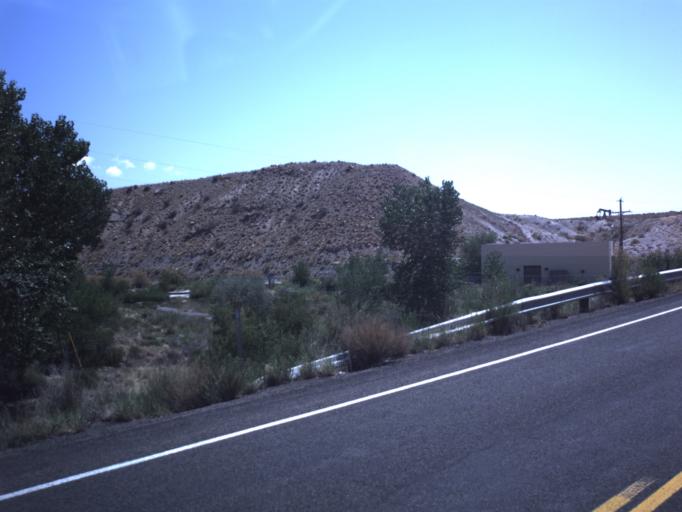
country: US
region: Utah
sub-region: Emery County
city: Orangeville
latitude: 39.2487
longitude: -111.0944
